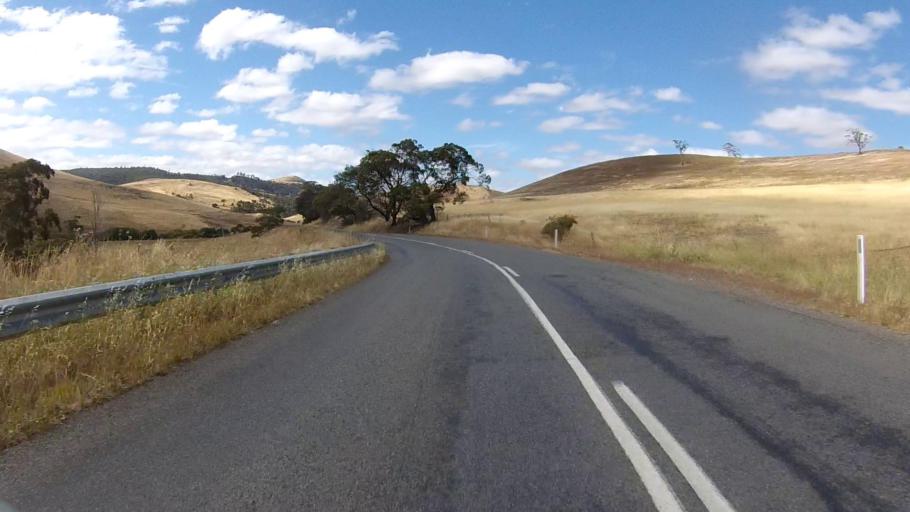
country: AU
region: Tasmania
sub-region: Brighton
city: Bridgewater
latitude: -42.5738
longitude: 147.4001
